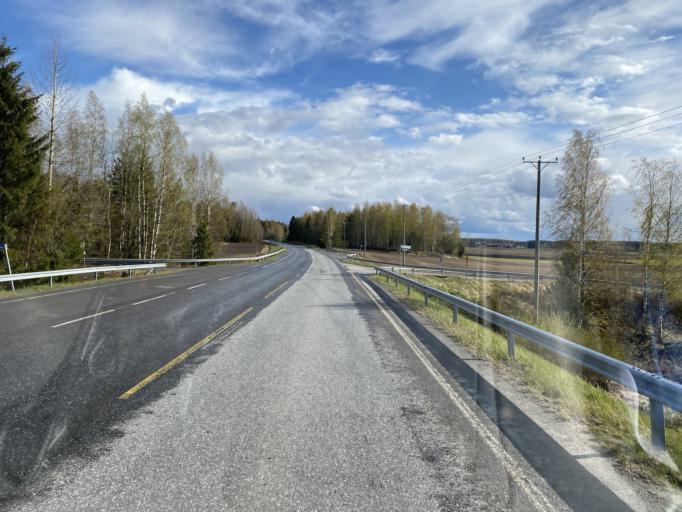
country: FI
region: Pirkanmaa
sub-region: Etelae-Pirkanmaa
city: Viiala
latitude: 61.2442
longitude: 23.7384
